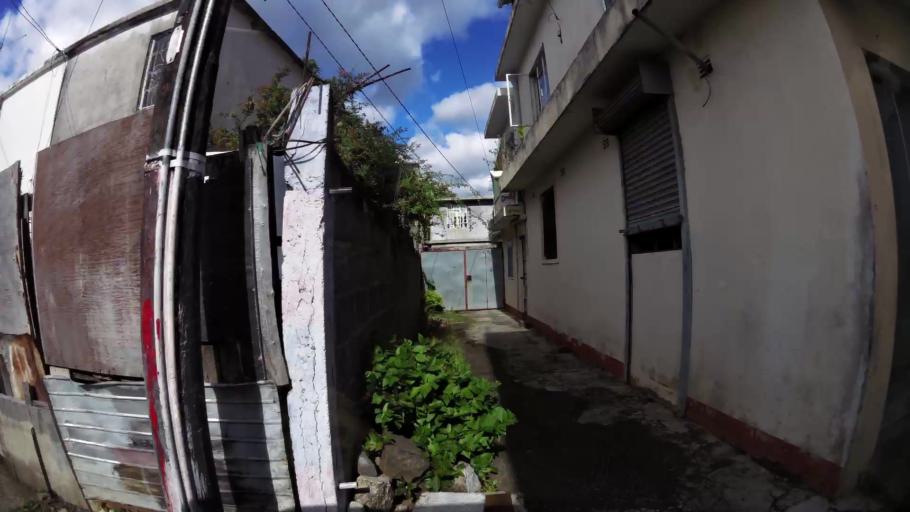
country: MU
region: Pamplemousses
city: Le Hochet
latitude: -20.1531
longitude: 57.5168
